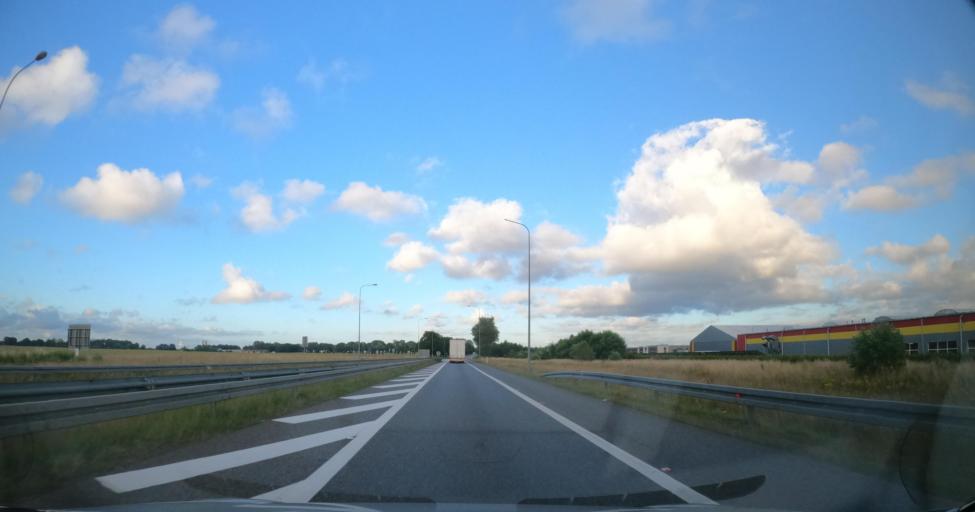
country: PL
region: Pomeranian Voivodeship
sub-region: Powiat slupski
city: Debnica Kaszubska
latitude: 54.4689
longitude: 17.1378
